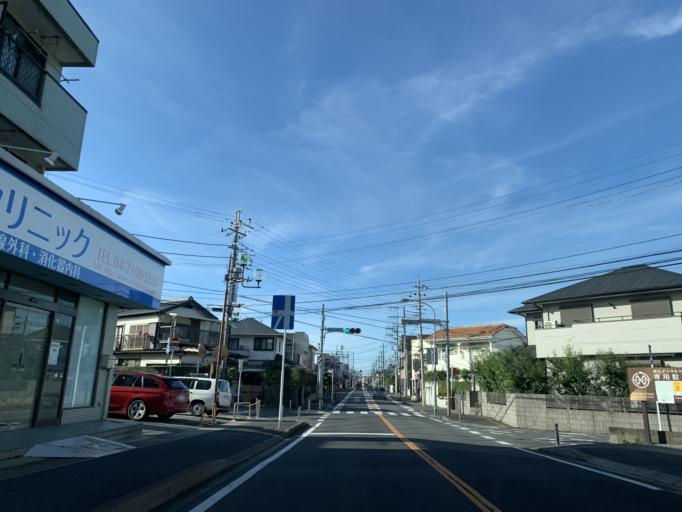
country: JP
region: Chiba
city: Nagareyama
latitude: 35.8826
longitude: 139.9239
